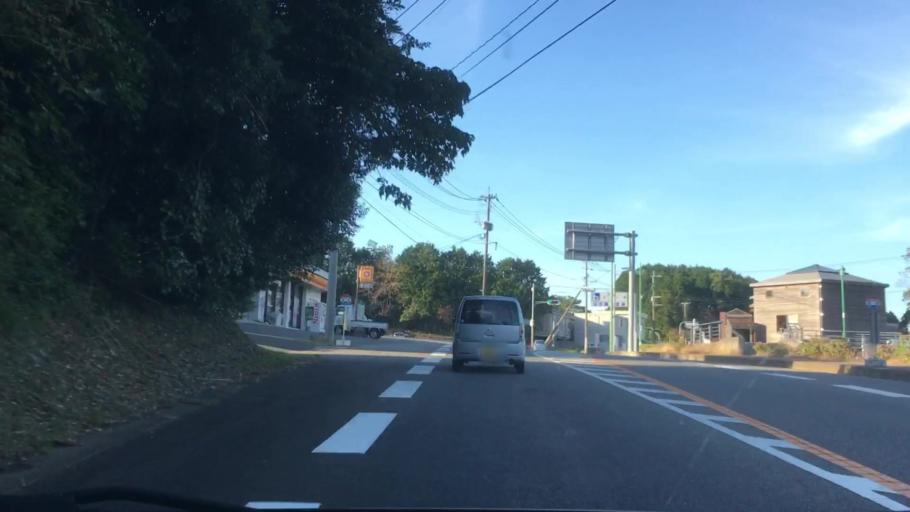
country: JP
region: Nagasaki
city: Sasebo
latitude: 33.0426
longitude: 129.6957
